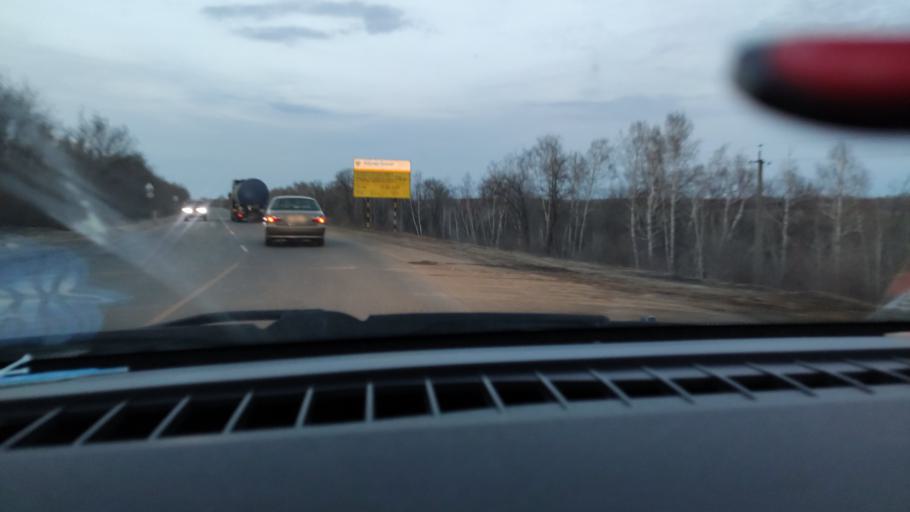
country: RU
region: Saratov
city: Sinodskoye
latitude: 52.0257
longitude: 46.7145
